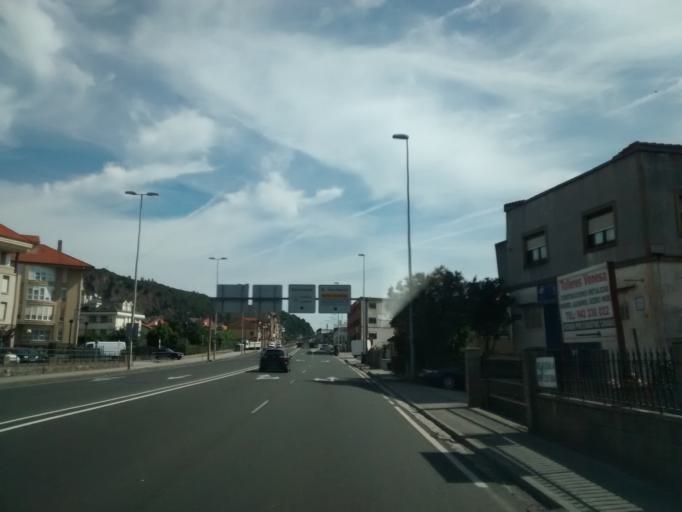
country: ES
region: Cantabria
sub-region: Provincia de Cantabria
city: Camargo
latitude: 43.4410
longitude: -3.8593
